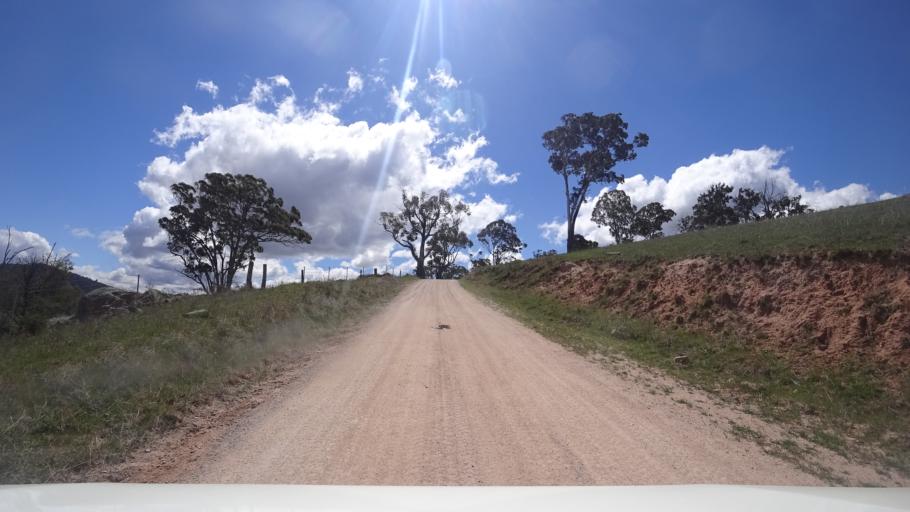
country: AU
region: New South Wales
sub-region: Oberon
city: Oberon
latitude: -33.5726
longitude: 149.9414
